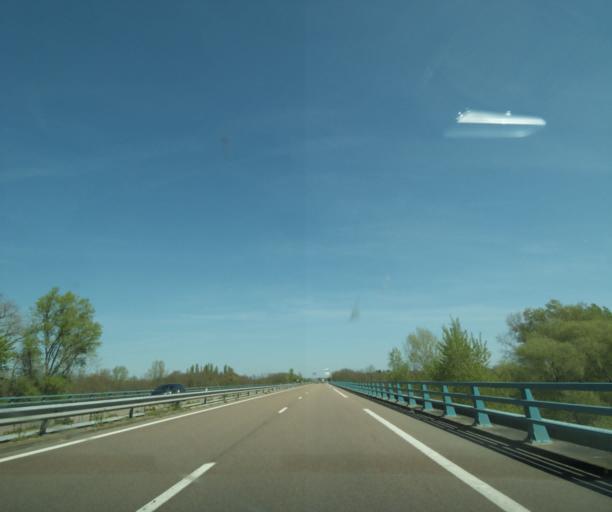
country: FR
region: Bourgogne
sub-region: Departement de la Nievre
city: Saint-Eloi
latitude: 46.9738
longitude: 3.1966
